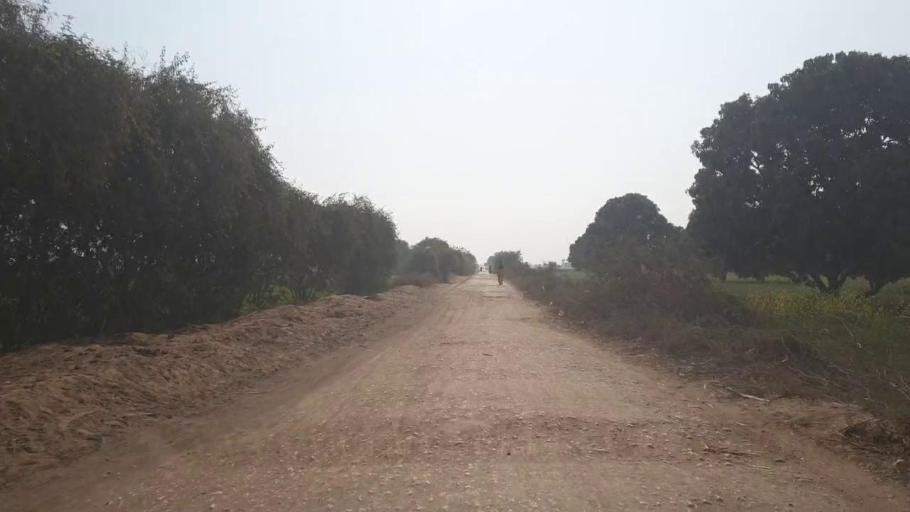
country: PK
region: Sindh
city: Tando Allahyar
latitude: 25.4815
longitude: 68.8024
